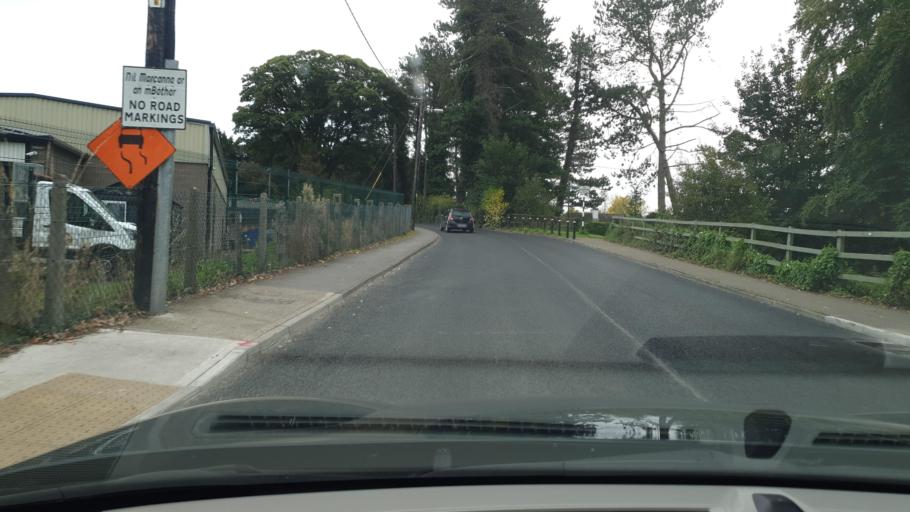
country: IE
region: Leinster
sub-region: Kildare
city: Naas
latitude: 53.2181
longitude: -6.6595
